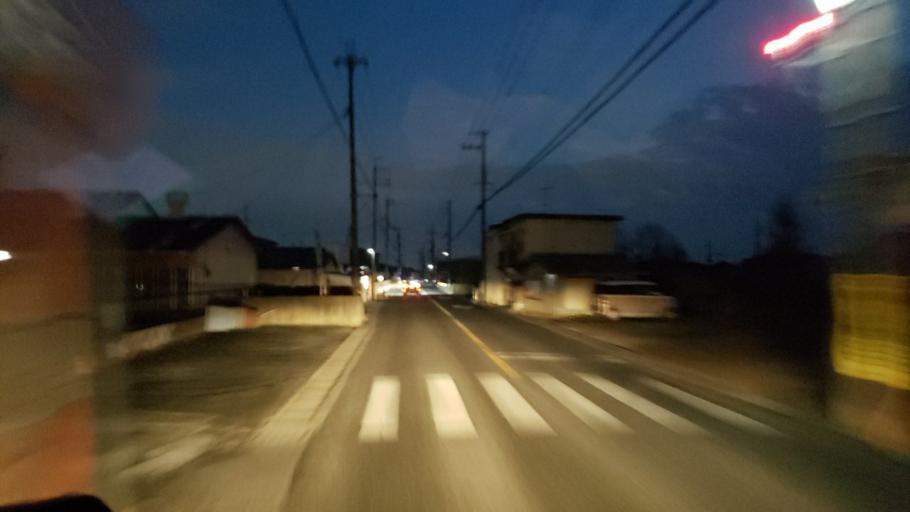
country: JP
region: Hyogo
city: Kakogawacho-honmachi
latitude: 34.8130
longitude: 134.8183
